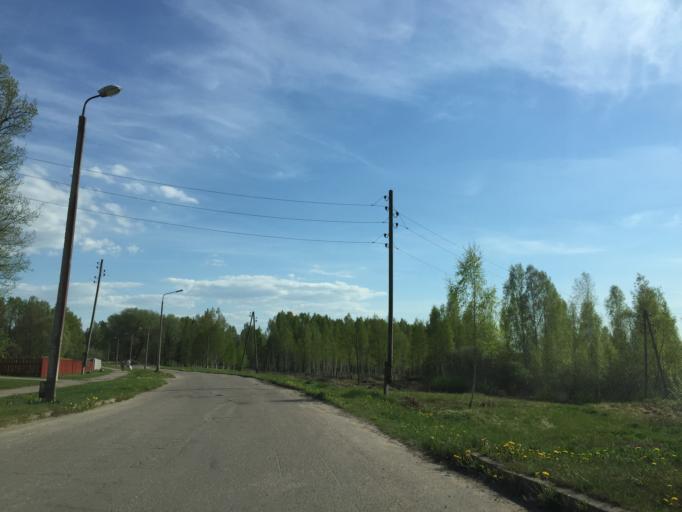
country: LV
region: Limbazu Rajons
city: Limbazi
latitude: 57.5083
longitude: 24.7055
